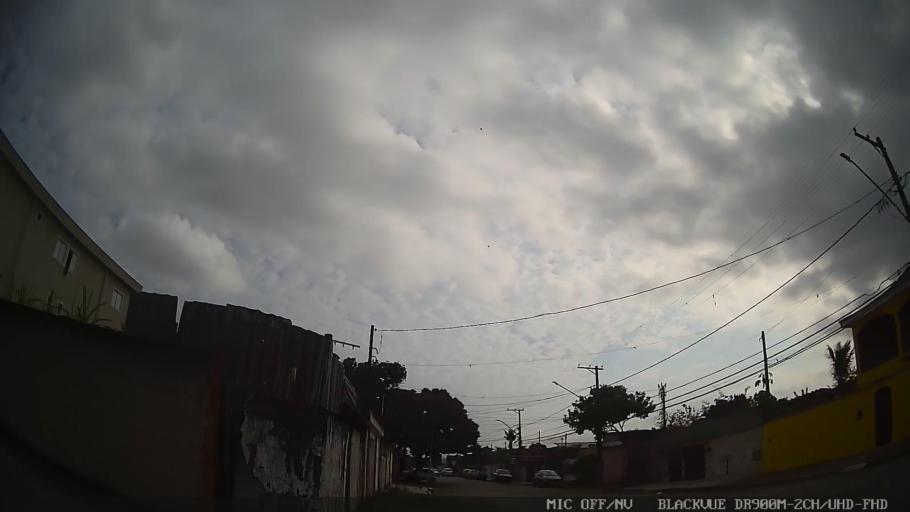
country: BR
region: Sao Paulo
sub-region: Guaruja
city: Guaruja
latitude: -23.9579
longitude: -46.2850
